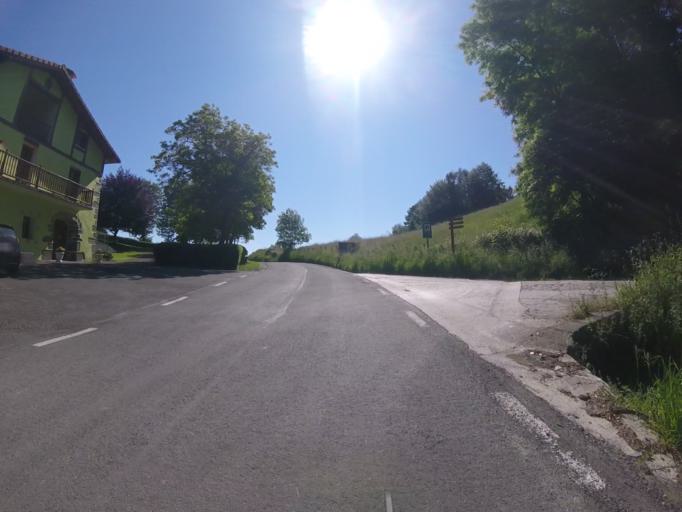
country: ES
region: Basque Country
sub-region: Provincia de Guipuzcoa
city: Beizama
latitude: 43.1225
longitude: -2.1838
